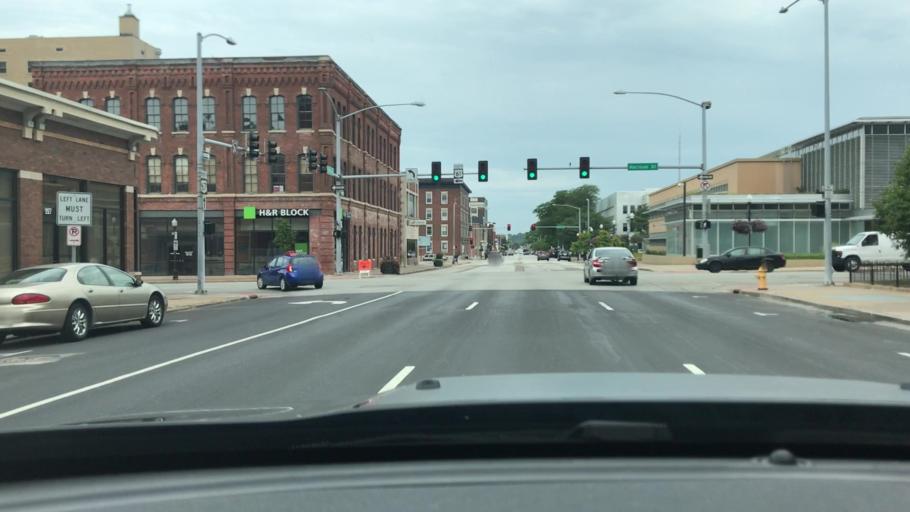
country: US
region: Iowa
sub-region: Scott County
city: Davenport
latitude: 41.5235
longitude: -90.5767
